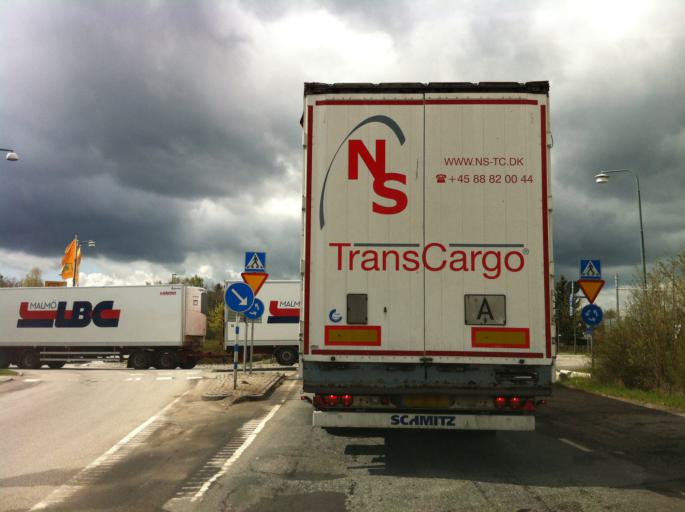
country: SE
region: Skane
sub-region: Hoors Kommun
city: Satofta
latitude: 55.9270
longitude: 13.5467
